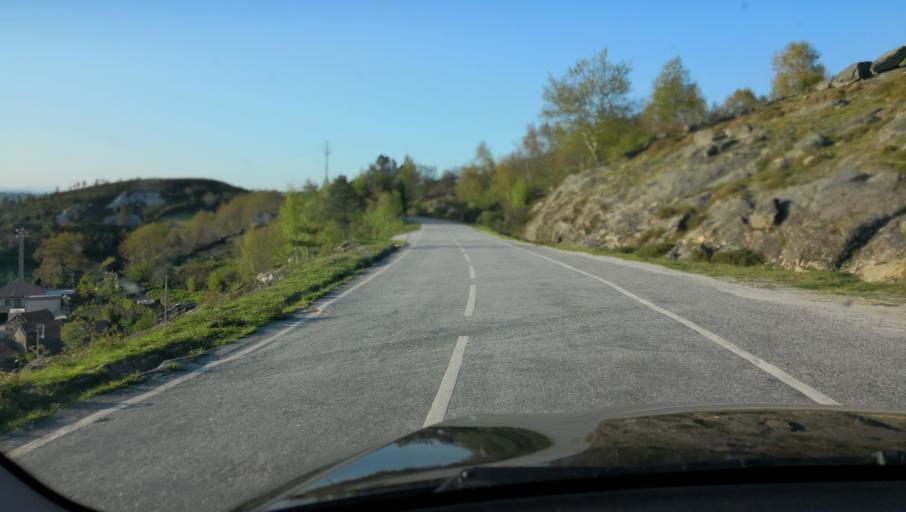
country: PT
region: Vila Real
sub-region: Vila Real
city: Vila Real
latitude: 41.3926
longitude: -7.8268
